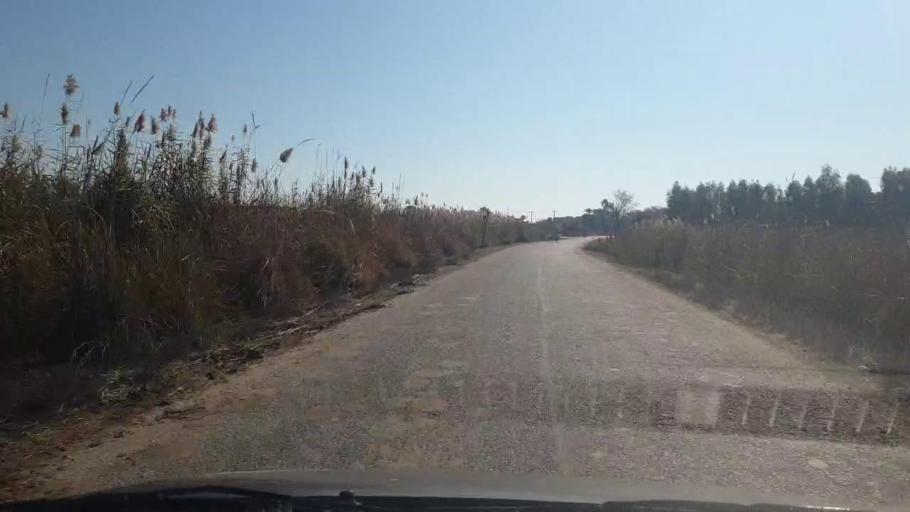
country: PK
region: Sindh
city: Bozdar
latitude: 27.1560
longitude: 68.6534
